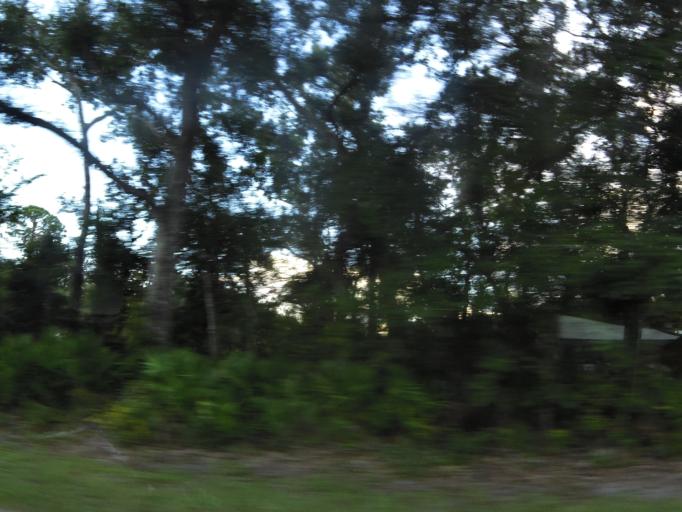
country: US
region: Georgia
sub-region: Camden County
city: St Marys
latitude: 30.7440
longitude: -81.5698
